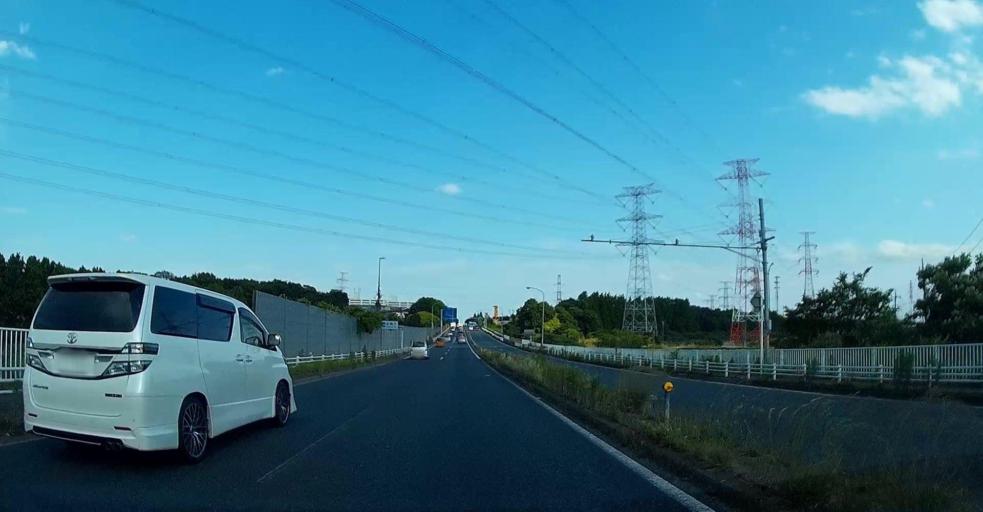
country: JP
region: Chiba
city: Shiroi
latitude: 35.7922
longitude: 140.0665
